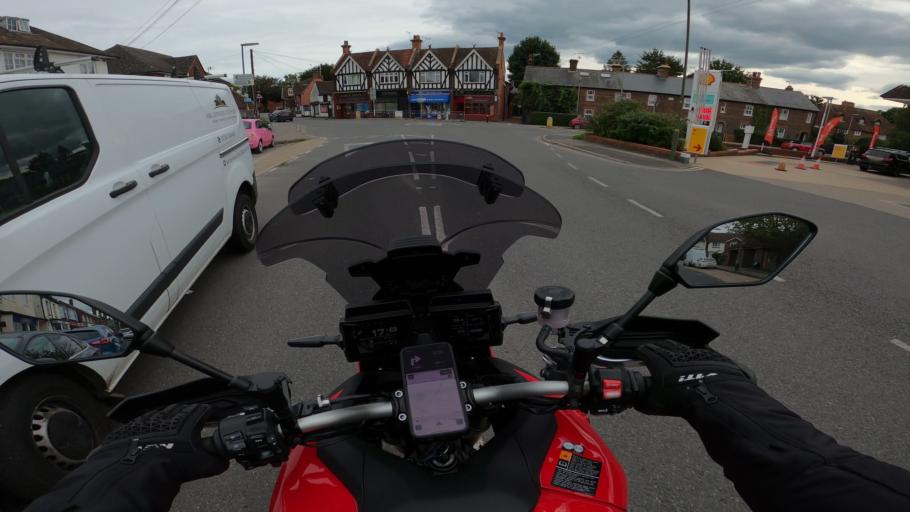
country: GB
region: England
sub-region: Surrey
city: Lingfield
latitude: 51.1753
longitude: -0.0207
